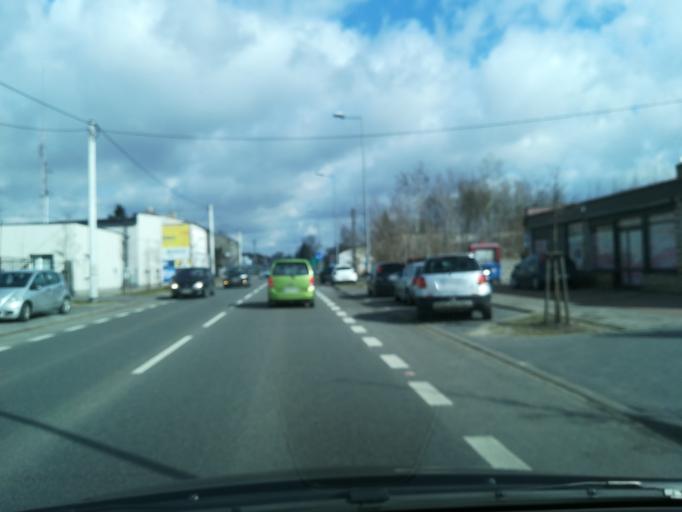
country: PL
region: Silesian Voivodeship
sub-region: Czestochowa
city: Czestochowa
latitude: 50.8220
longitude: 19.1326
